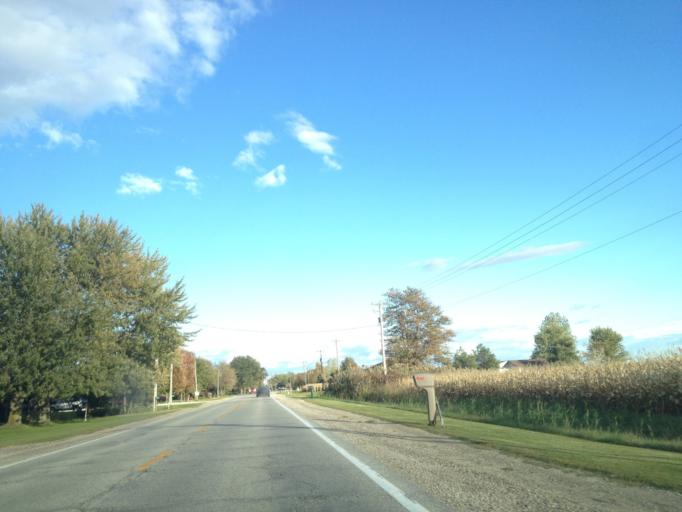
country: US
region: Michigan
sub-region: Wayne County
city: Grosse Pointe Farms
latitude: 42.2969
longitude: -82.6565
